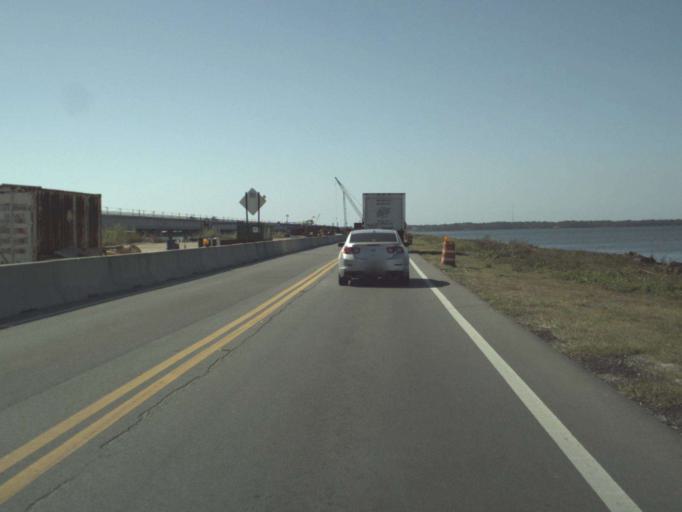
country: US
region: Florida
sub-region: Walton County
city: Freeport
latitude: 30.4227
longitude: -86.1582
